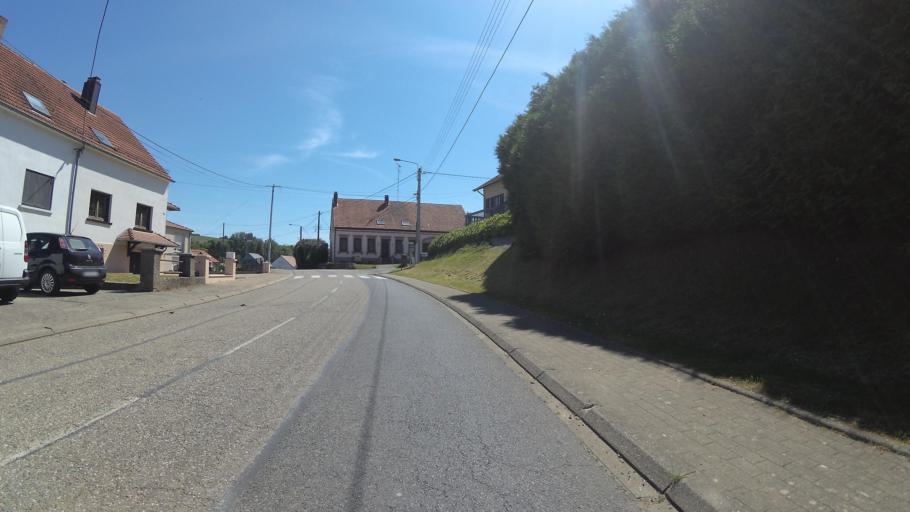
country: FR
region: Lorraine
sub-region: Departement de la Moselle
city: Bliesbruck
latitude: 49.1233
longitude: 7.1471
